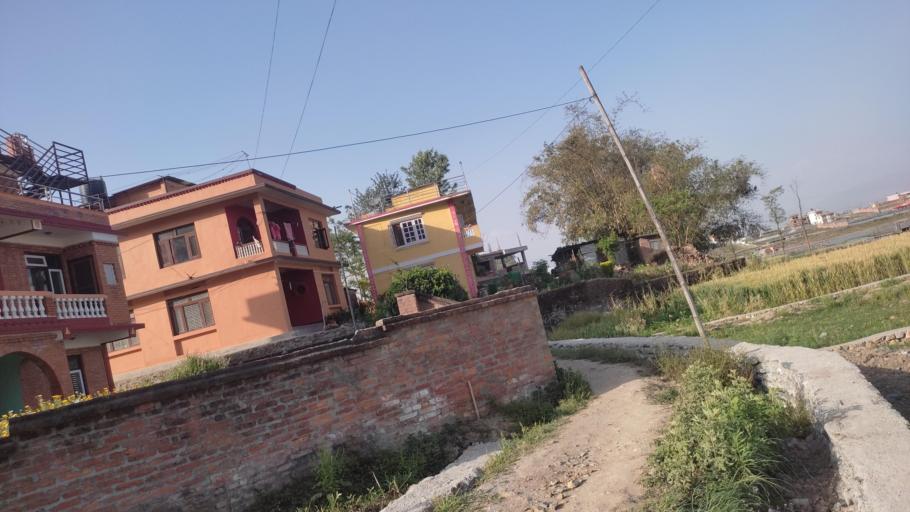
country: NP
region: Central Region
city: Kirtipur
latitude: 27.6594
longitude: 85.2703
